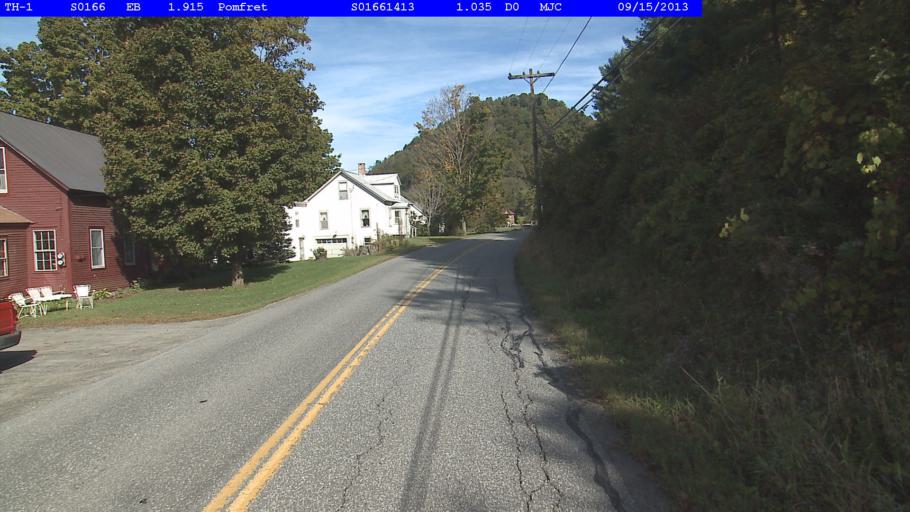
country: US
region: Vermont
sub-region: Windsor County
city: Woodstock
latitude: 43.6630
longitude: -72.5379
